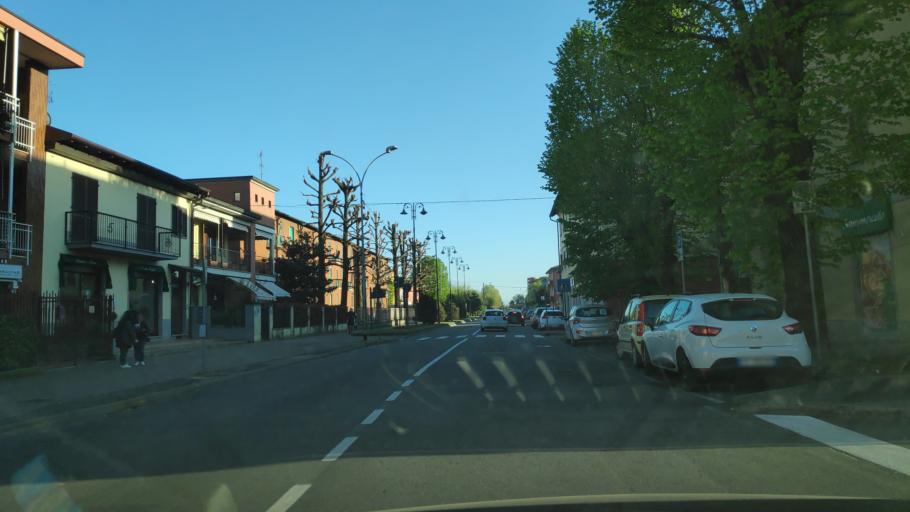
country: IT
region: Lombardy
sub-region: Citta metropolitana di Milano
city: Pieve Emanuele
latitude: 45.3566
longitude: 9.2015
